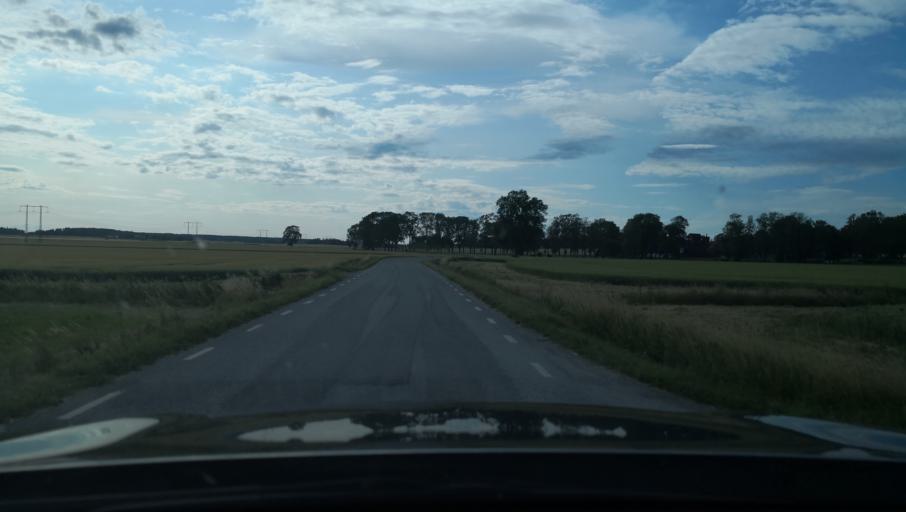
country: SE
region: Uppsala
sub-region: Enkopings Kommun
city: Orsundsbro
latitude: 59.6959
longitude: 17.3274
